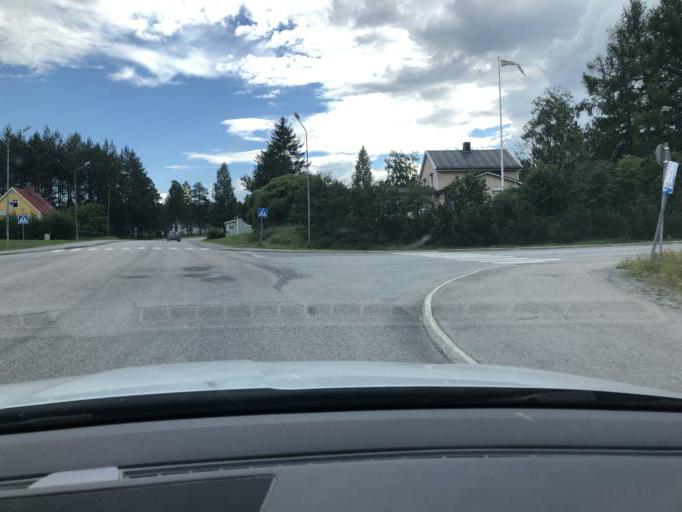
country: SE
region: Vaesternorrland
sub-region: Solleftea Kommun
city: Solleftea
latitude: 63.1768
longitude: 17.0586
